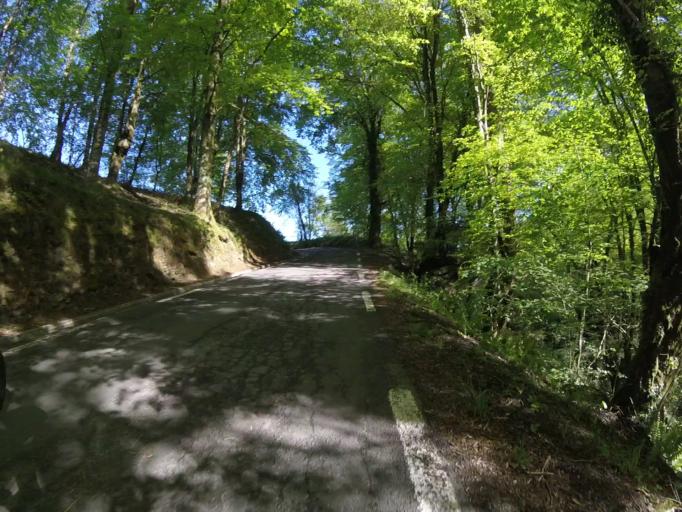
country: ES
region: Basque Country
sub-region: Provincia de Guipuzcoa
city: Aizarnazabal
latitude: 43.2180
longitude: -2.2126
